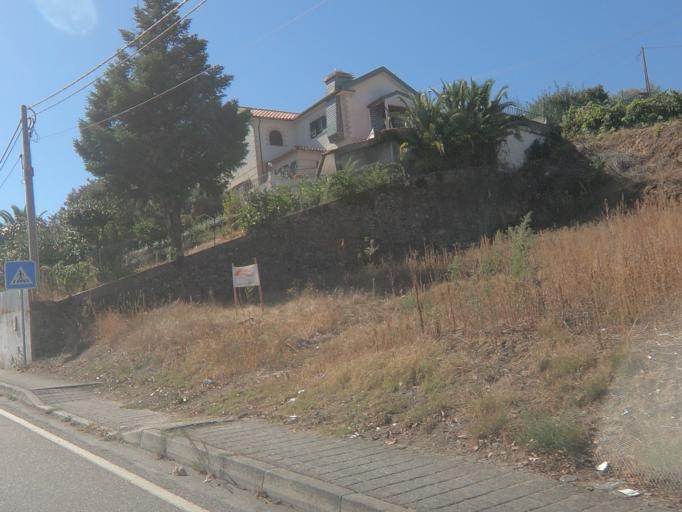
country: PT
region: Vila Real
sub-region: Vila Real
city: Vila Real
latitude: 41.2831
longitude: -7.7596
